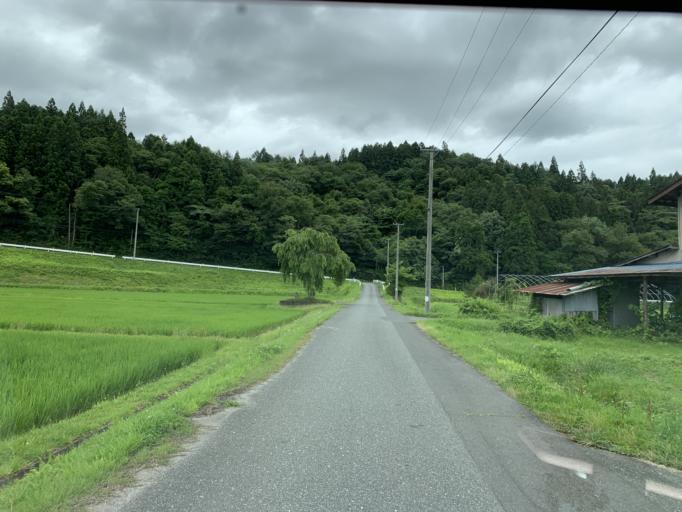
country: JP
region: Iwate
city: Ichinoseki
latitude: 38.9137
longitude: 141.0761
